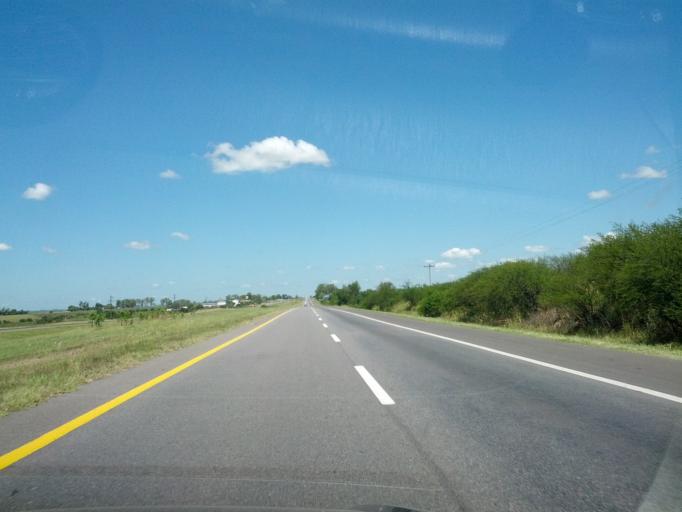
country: AR
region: Entre Rios
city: Gualeguaychu
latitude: -33.0920
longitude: -58.6406
